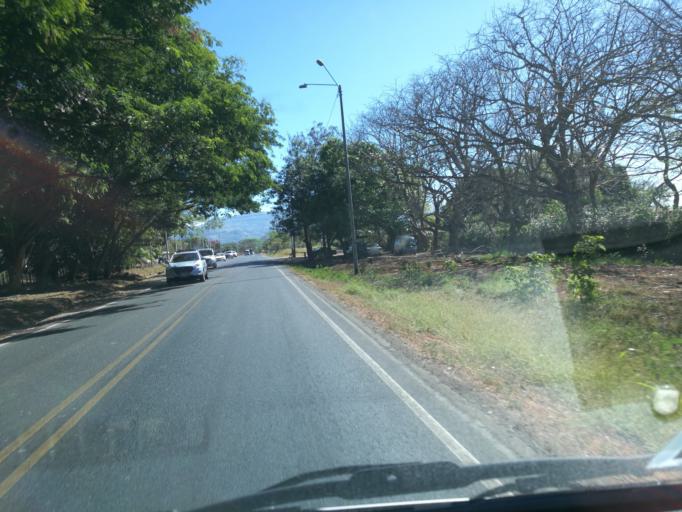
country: CR
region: Puntarenas
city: Miramar
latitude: 10.0935
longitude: -84.8220
